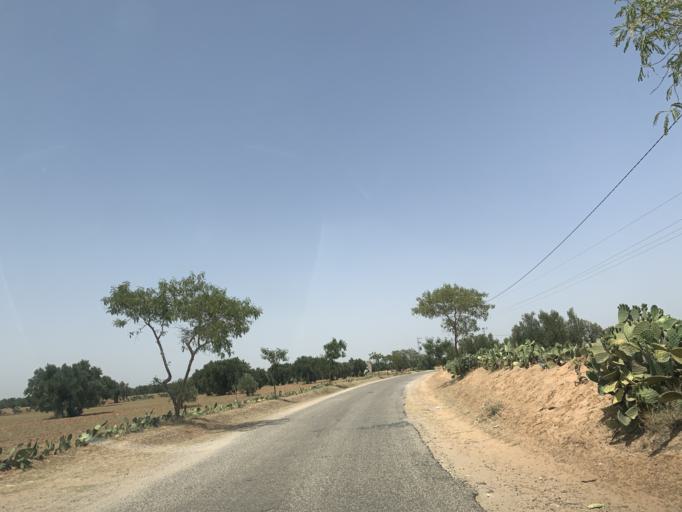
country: TN
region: Al Mahdiyah
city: Shurban
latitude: 35.1868
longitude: 10.2433
